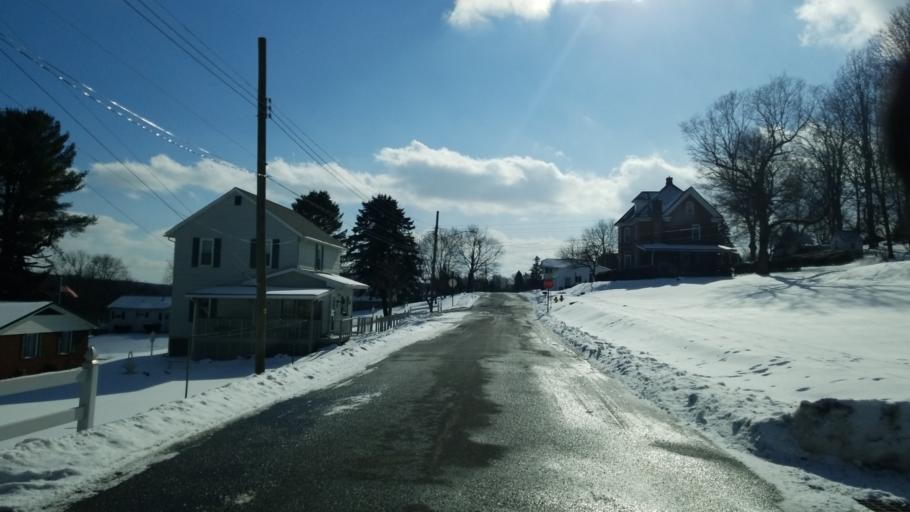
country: US
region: Pennsylvania
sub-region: Jefferson County
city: Falls Creek
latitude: 41.1427
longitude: -78.8064
